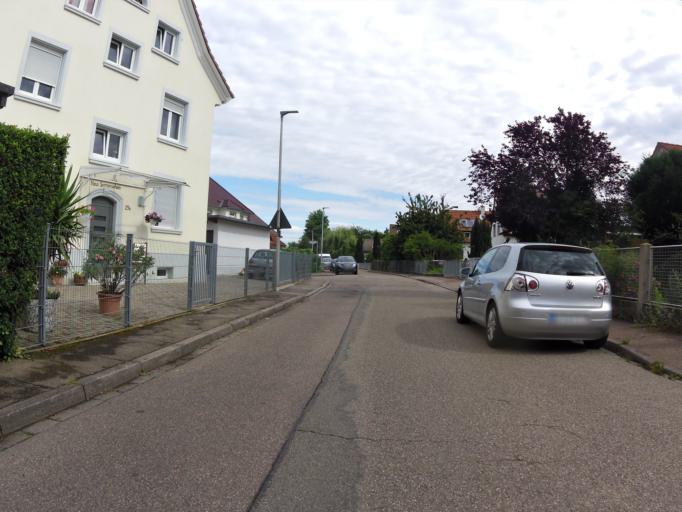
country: DE
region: Baden-Wuerttemberg
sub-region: Freiburg Region
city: Lahr
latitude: 48.3483
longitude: 7.8365
